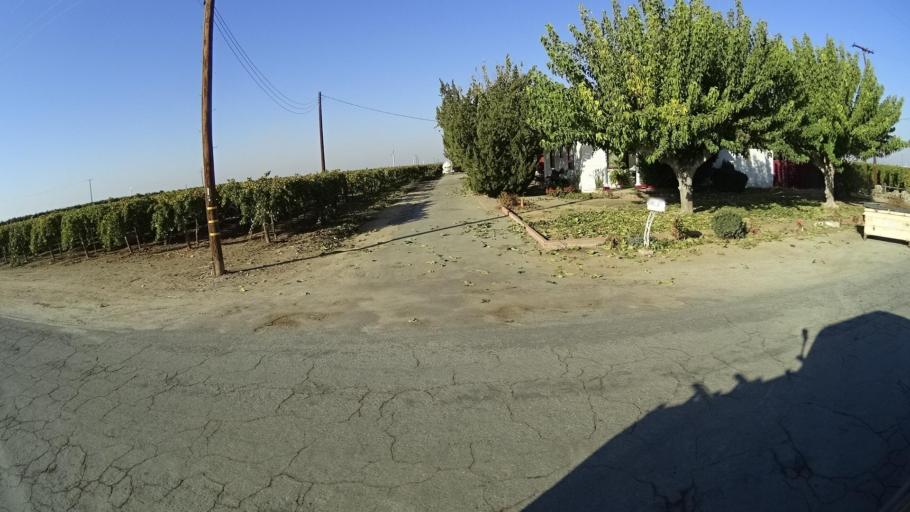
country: US
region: California
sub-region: Tulare County
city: Richgrove
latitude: 35.7708
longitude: -119.1493
